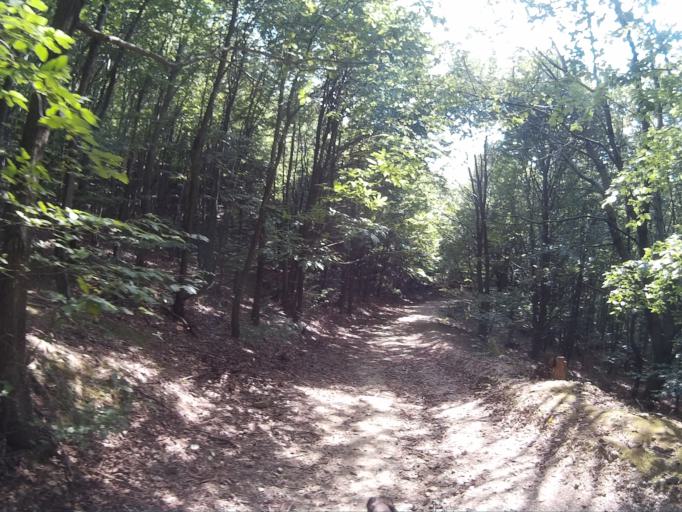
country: HU
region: Vas
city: Koszeg
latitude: 47.3910
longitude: 16.5028
